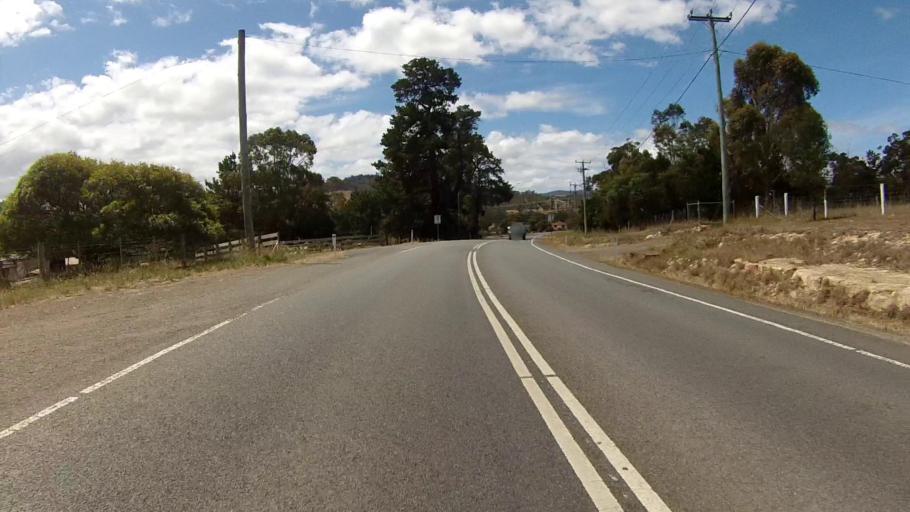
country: AU
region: Tasmania
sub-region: Sorell
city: Sorell
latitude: -42.8067
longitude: 147.6290
